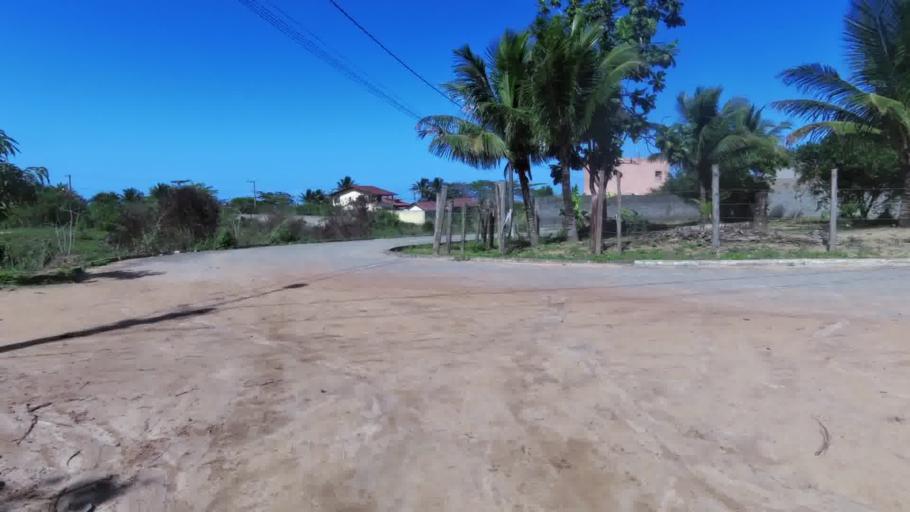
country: BR
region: Espirito Santo
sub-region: Piuma
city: Piuma
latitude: -20.8291
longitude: -40.6214
